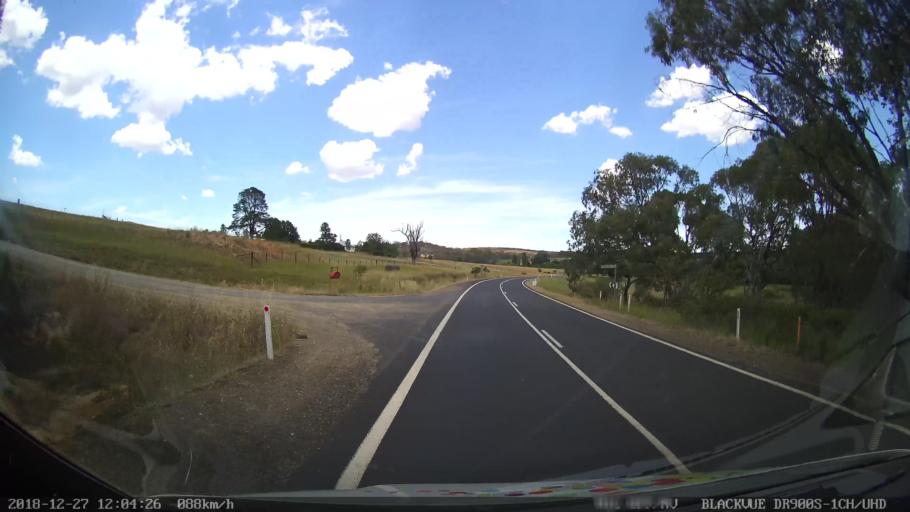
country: AU
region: New South Wales
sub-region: Blayney
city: Blayney
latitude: -33.7969
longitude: 149.3505
